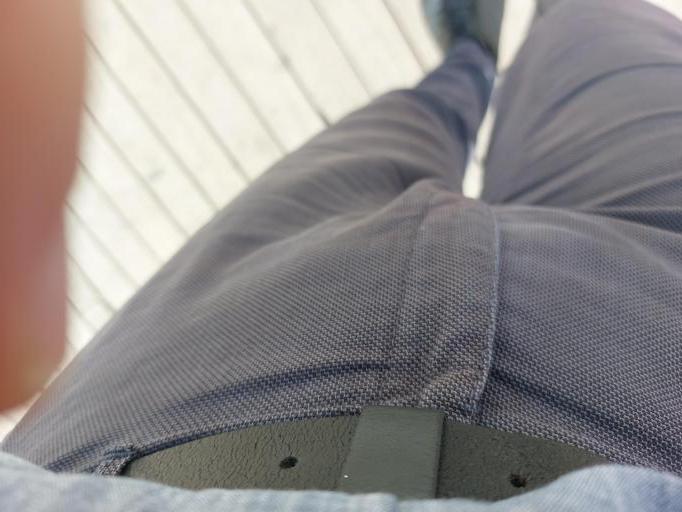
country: MA
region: Grand Casablanca
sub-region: Casablanca
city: Casablanca
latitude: 33.6081
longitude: -7.6211
